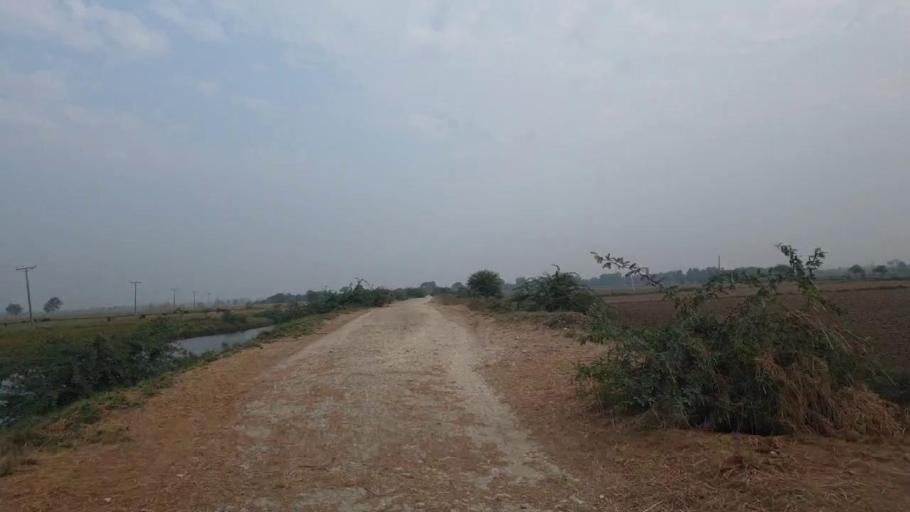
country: PK
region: Sindh
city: Talhar
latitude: 24.8223
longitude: 68.8781
